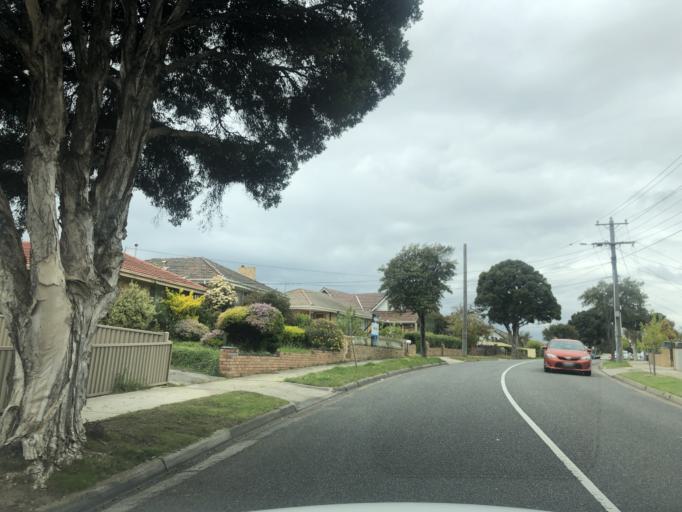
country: AU
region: Victoria
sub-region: Greater Dandenong
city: Noble Park North
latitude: -37.9608
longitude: 145.1958
